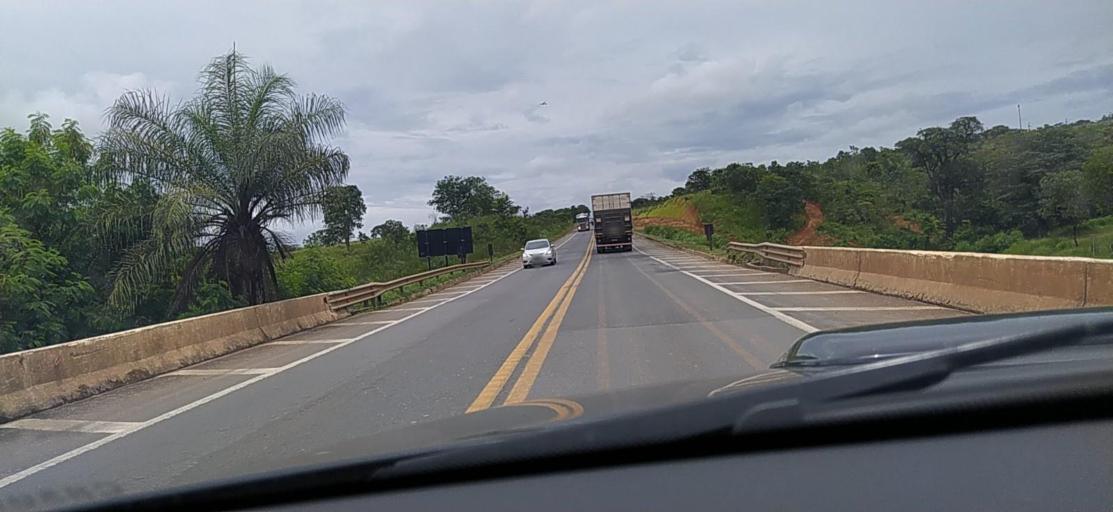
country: BR
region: Minas Gerais
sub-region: Curvelo
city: Curvelo
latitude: -18.7392
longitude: -44.4434
